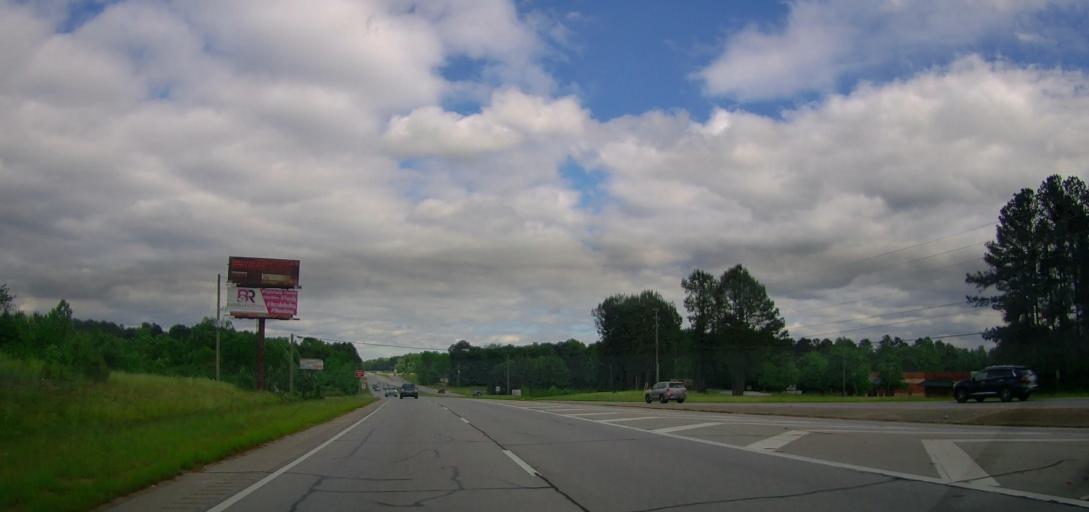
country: US
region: Georgia
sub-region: Walton County
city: Monroe
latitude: 33.8097
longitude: -83.7969
